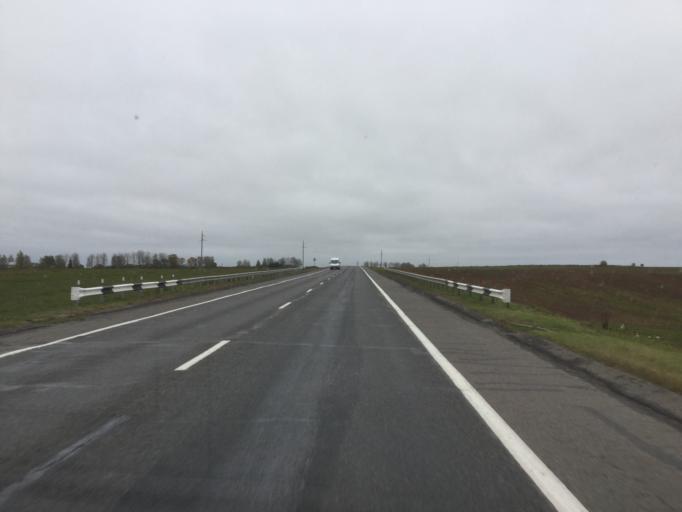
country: BY
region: Vitebsk
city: Chashniki
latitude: 55.0100
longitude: 29.1601
